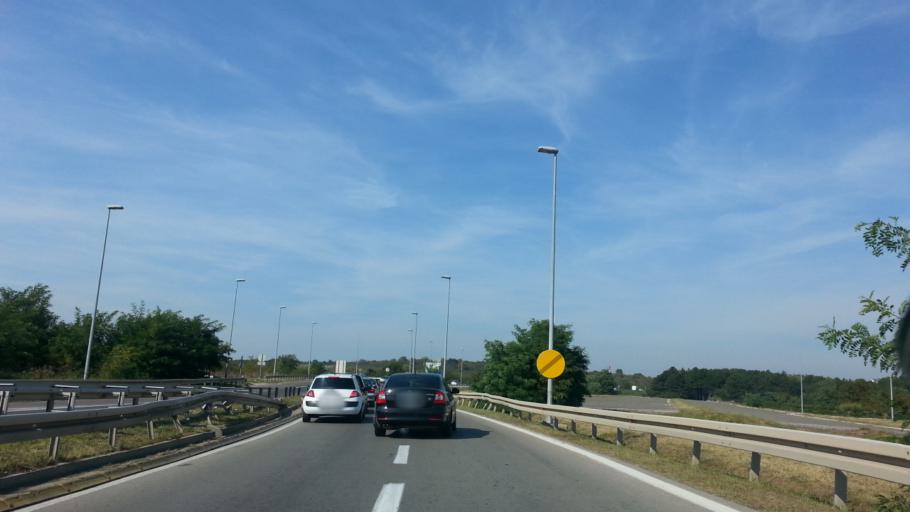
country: RS
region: Central Serbia
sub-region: Belgrade
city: Rakovica
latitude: 44.7158
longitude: 20.4159
